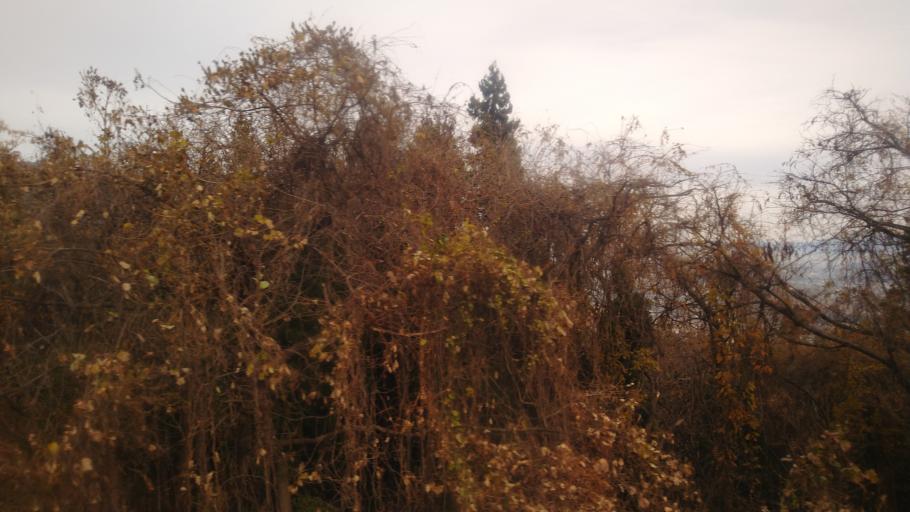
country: JP
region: Nagano
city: Nagano-shi
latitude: 36.5080
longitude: 138.0871
